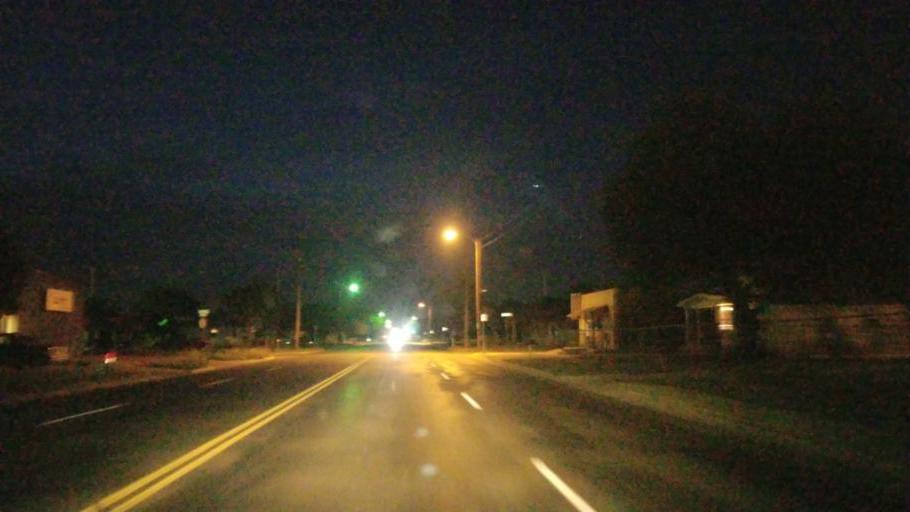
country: US
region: Texas
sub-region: Potter County
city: Amarillo
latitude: 35.1972
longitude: -101.8262
